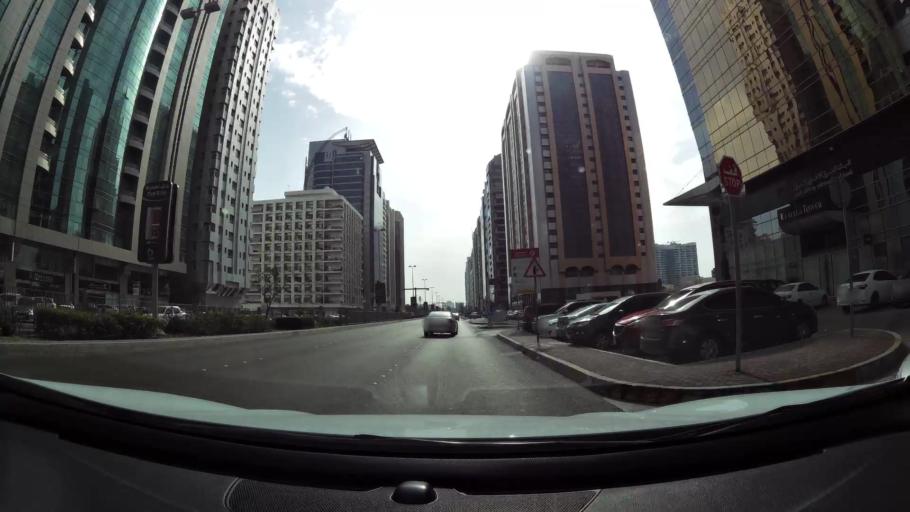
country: AE
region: Abu Dhabi
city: Abu Dhabi
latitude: 24.4734
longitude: 54.3477
